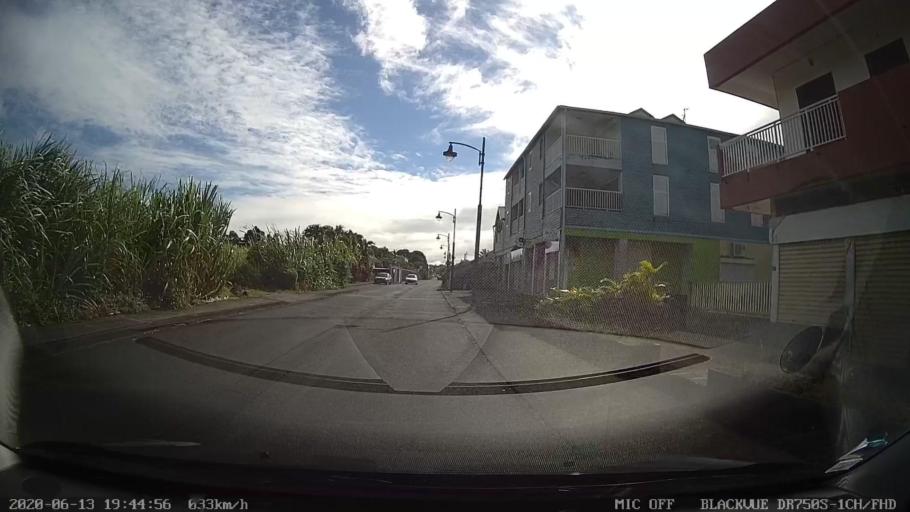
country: RE
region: Reunion
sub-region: Reunion
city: Bras-Panon
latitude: -20.9994
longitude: 55.6767
